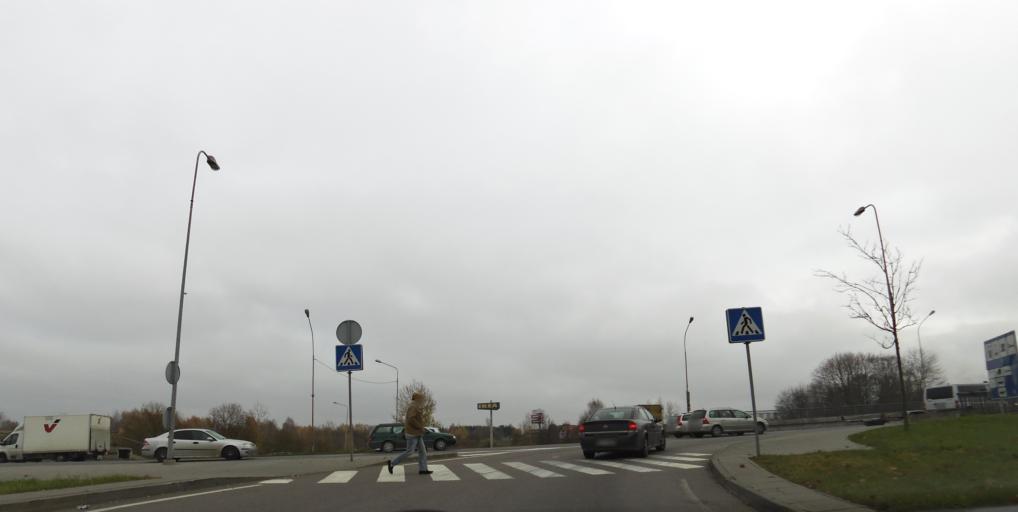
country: LT
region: Vilnius County
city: Naujamiestis
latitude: 54.6560
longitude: 25.2713
